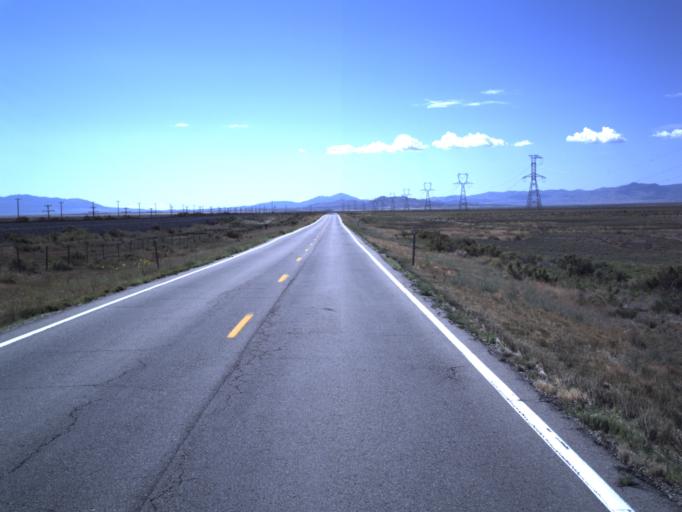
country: US
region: Utah
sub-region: Tooele County
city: Tooele
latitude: 40.3017
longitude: -112.4028
